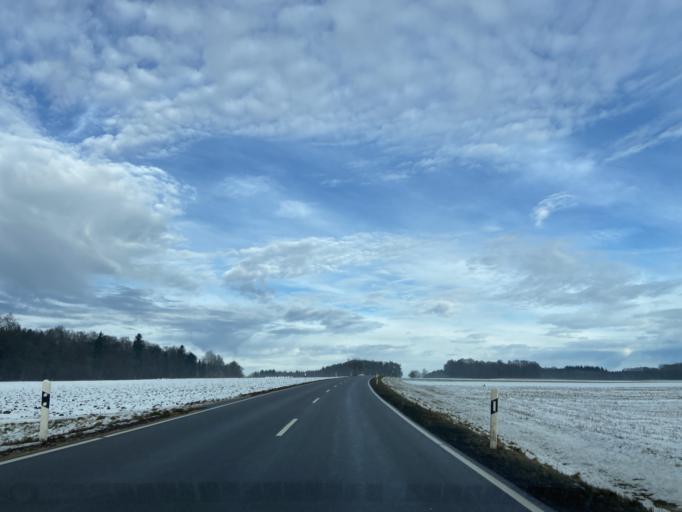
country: DE
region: Baden-Wuerttemberg
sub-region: Tuebingen Region
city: Hettingen
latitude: 48.2034
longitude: 9.2822
